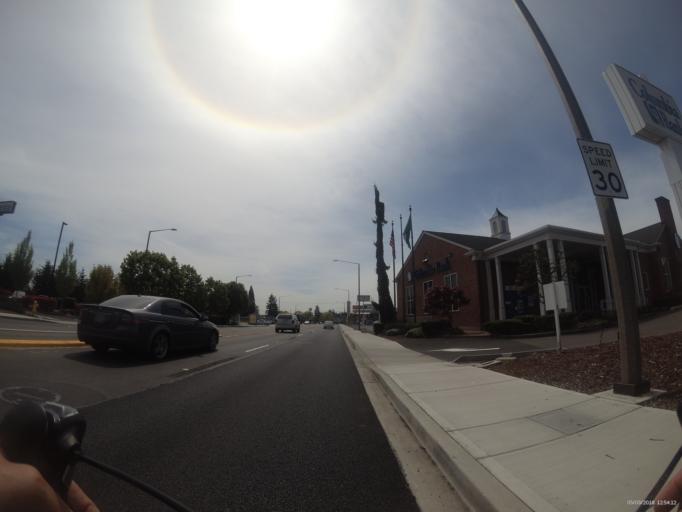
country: US
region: Washington
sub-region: Pierce County
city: Lakewood
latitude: 47.1699
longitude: -122.5200
